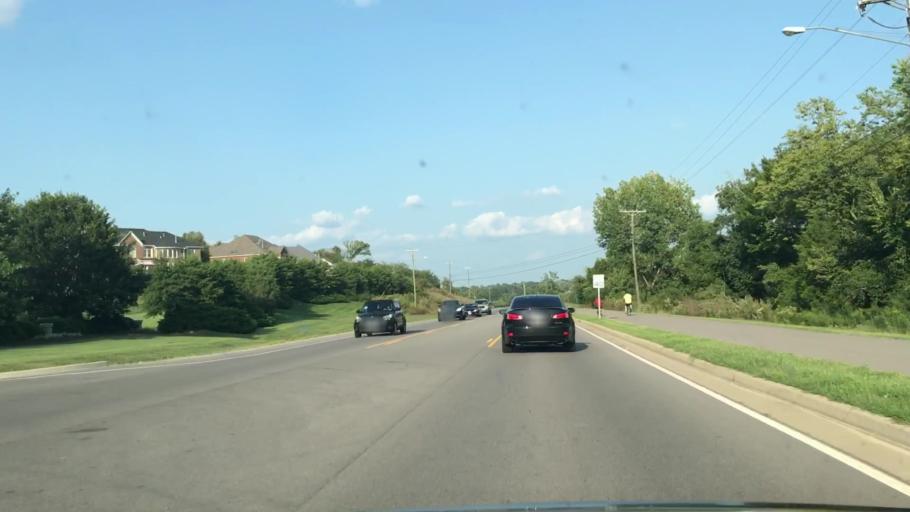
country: US
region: Tennessee
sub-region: Williamson County
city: Nolensville
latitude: 35.9854
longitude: -86.7140
